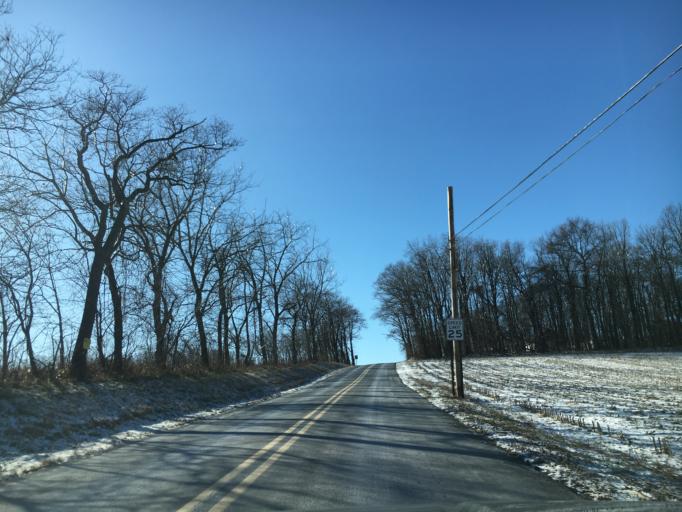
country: US
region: Pennsylvania
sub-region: Lehigh County
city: Egypt
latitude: 40.6862
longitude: -75.5667
